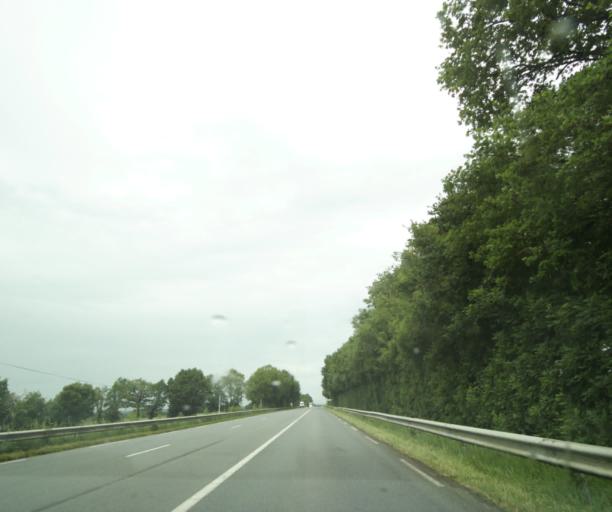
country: FR
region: Poitou-Charentes
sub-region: Departement des Deux-Sevres
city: Le Tallud
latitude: 46.6095
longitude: -0.2853
